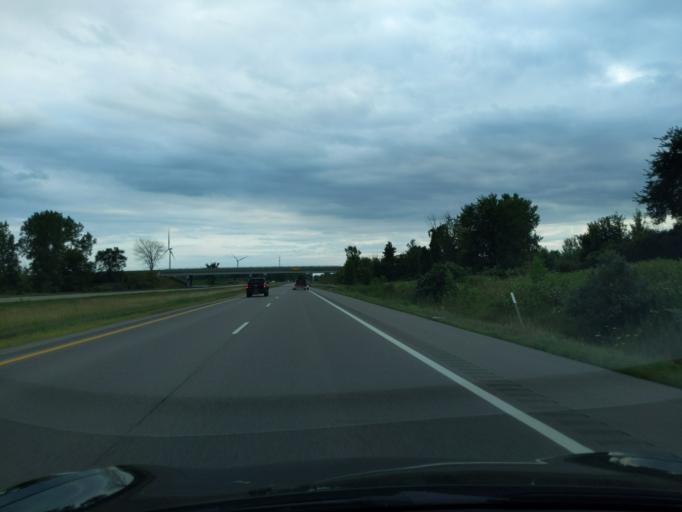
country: US
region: Michigan
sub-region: Isabella County
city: Shepherd
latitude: 43.5115
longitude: -84.6769
